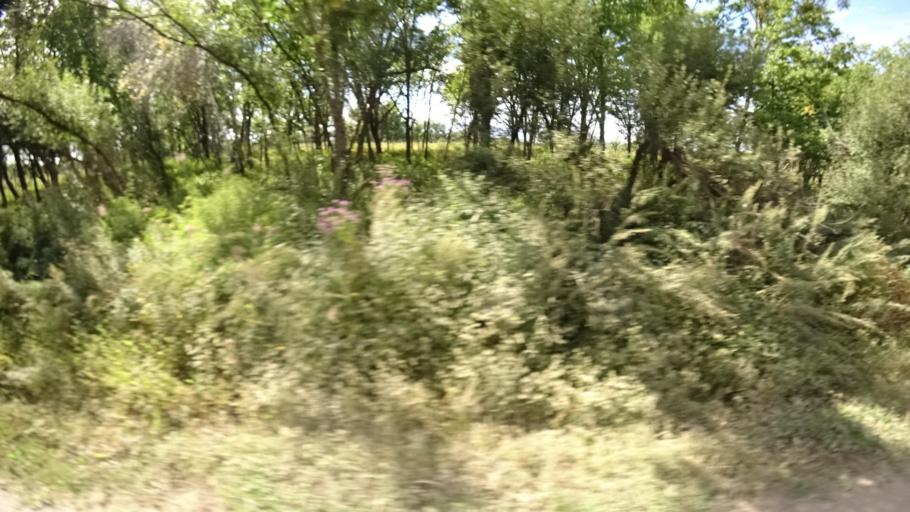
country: RU
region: Primorskiy
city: Yakovlevka
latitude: 44.3998
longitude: 133.5622
